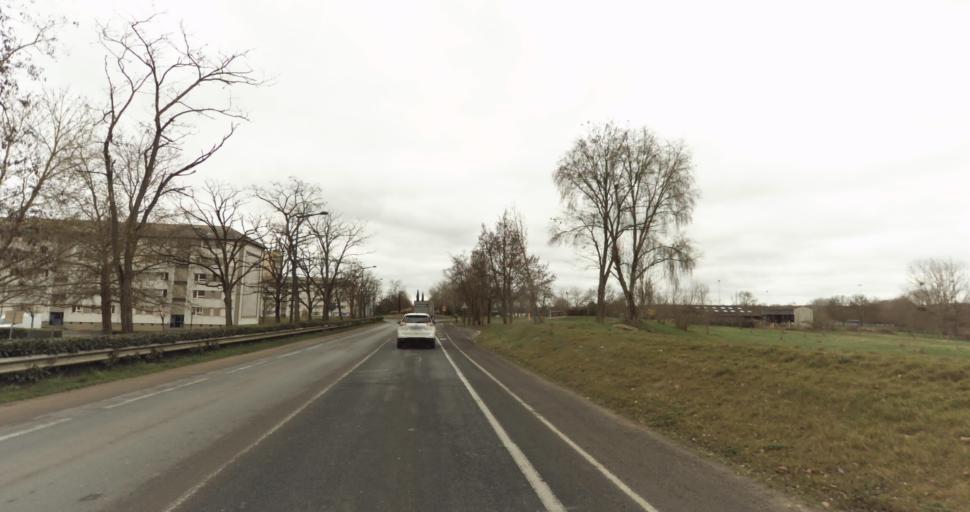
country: FR
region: Pays de la Loire
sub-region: Departement de Maine-et-Loire
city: Saumur
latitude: 47.2482
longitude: -0.0790
